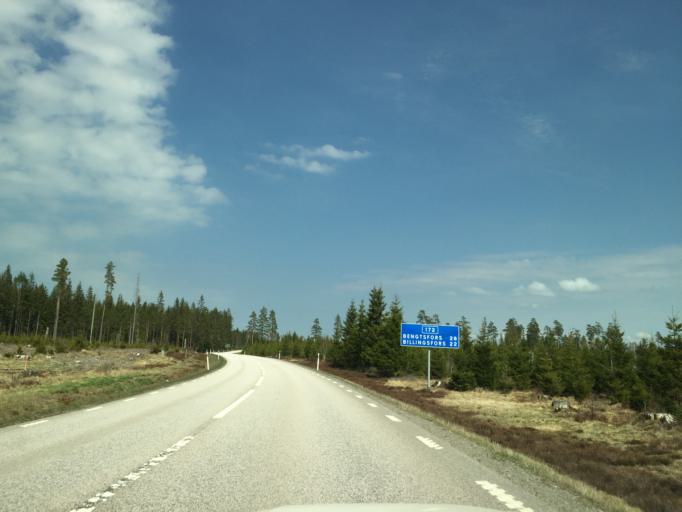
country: SE
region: Vaestra Goetaland
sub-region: Bengtsfors Kommun
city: Dals Langed
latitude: 58.8267
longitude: 12.1402
